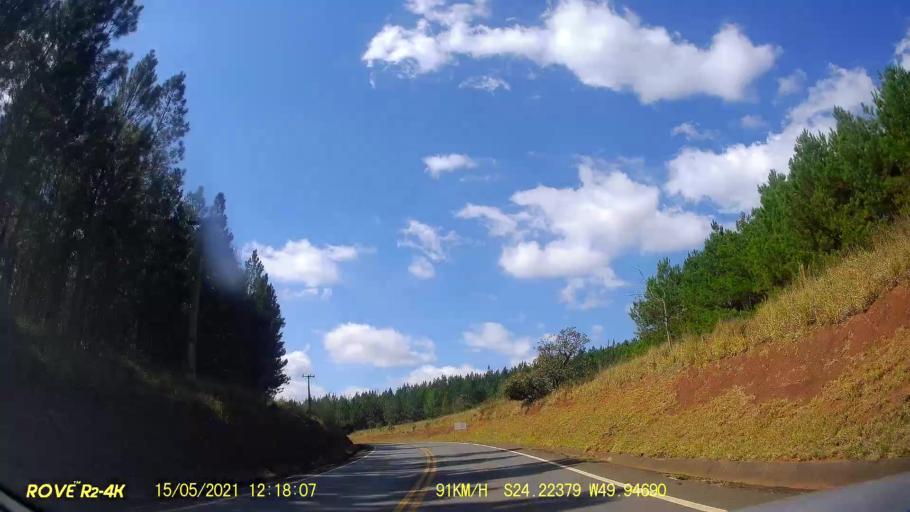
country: BR
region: Parana
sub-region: Jaguariaiva
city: Jaguariaiva
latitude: -24.2238
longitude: -49.9469
